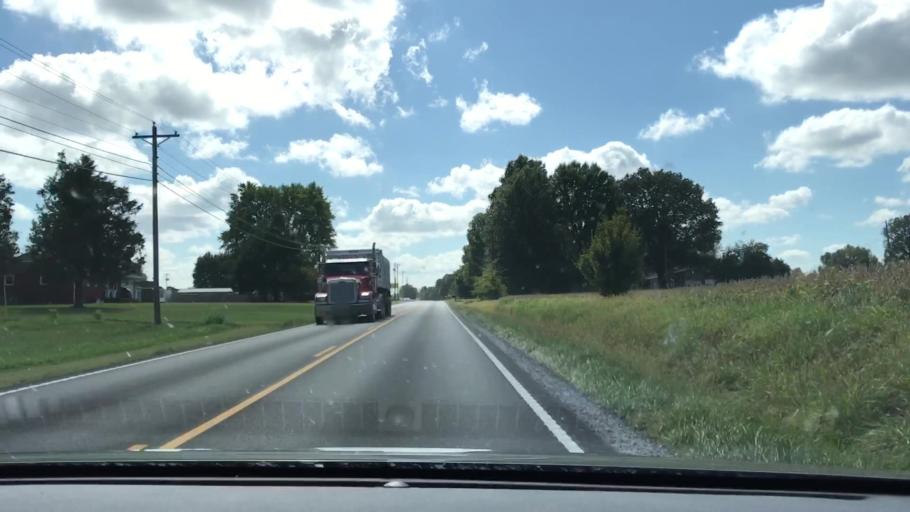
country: US
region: Kentucky
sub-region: Graves County
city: Mayfield
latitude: 36.7657
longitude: -88.5961
